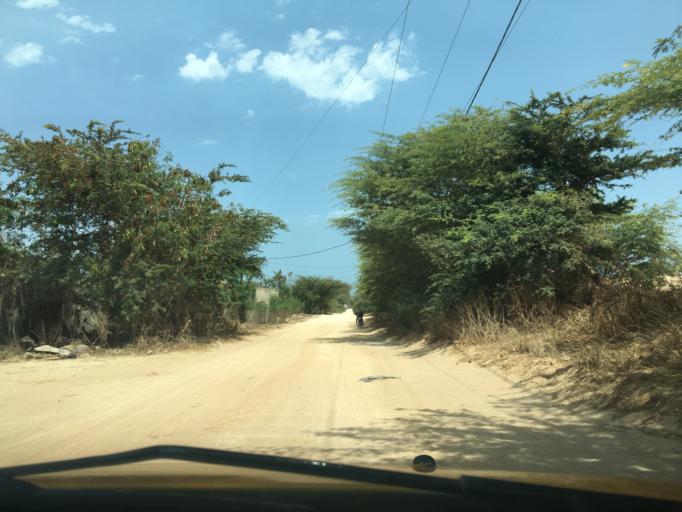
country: SN
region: Thies
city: Thies
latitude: 14.8211
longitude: -17.2017
